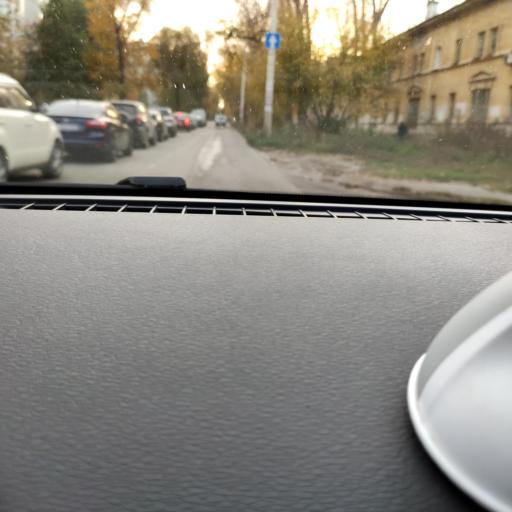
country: RU
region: Samara
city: Petra-Dubrava
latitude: 53.2280
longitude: 50.2723
